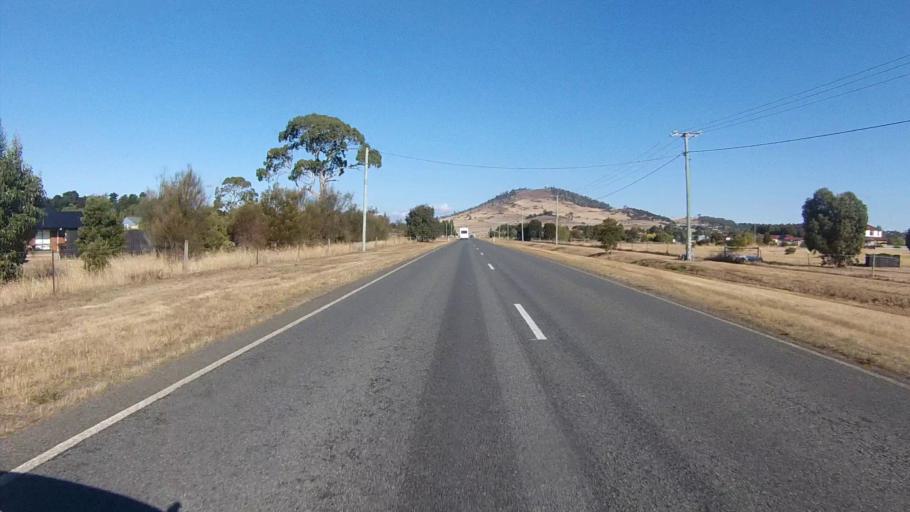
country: AU
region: Tasmania
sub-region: Clarence
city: Seven Mile Beach
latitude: -42.8551
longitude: 147.4886
